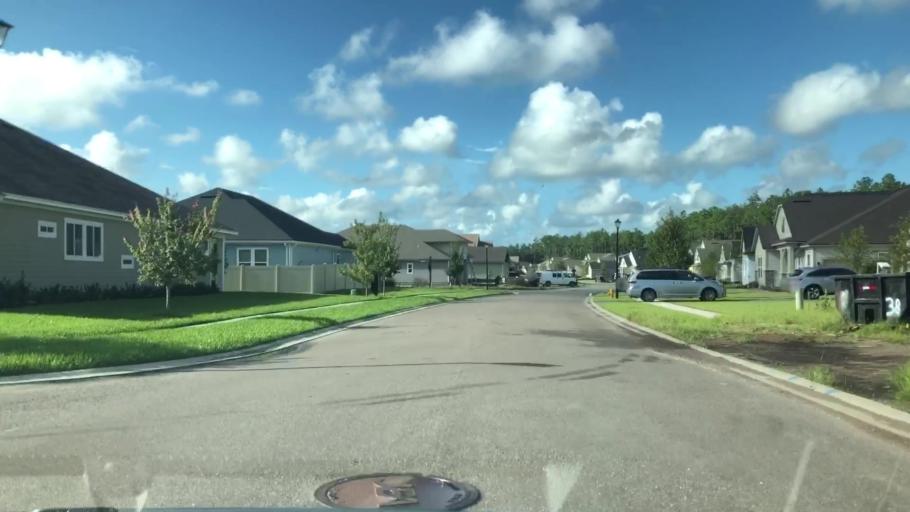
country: US
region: Florida
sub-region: Saint Johns County
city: Palm Valley
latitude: 30.1380
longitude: -81.4133
